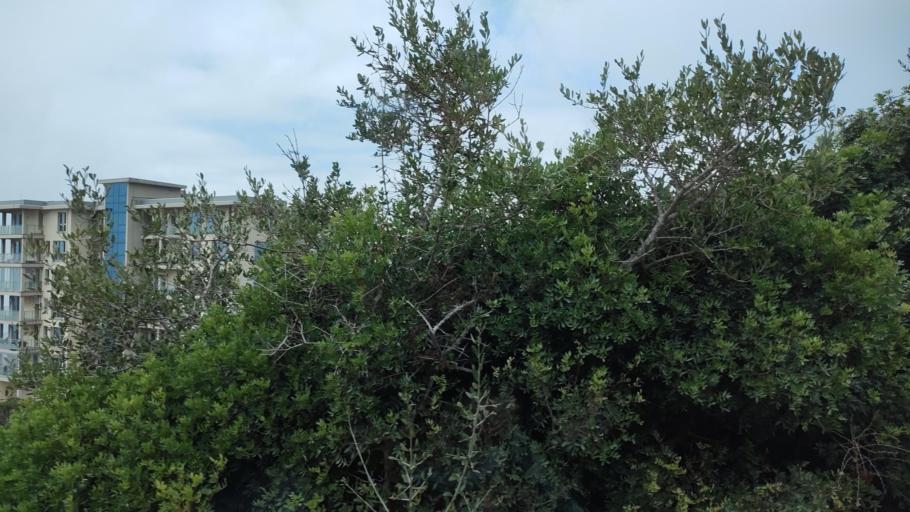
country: GI
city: Gibraltar
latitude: 36.1201
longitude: -5.3453
